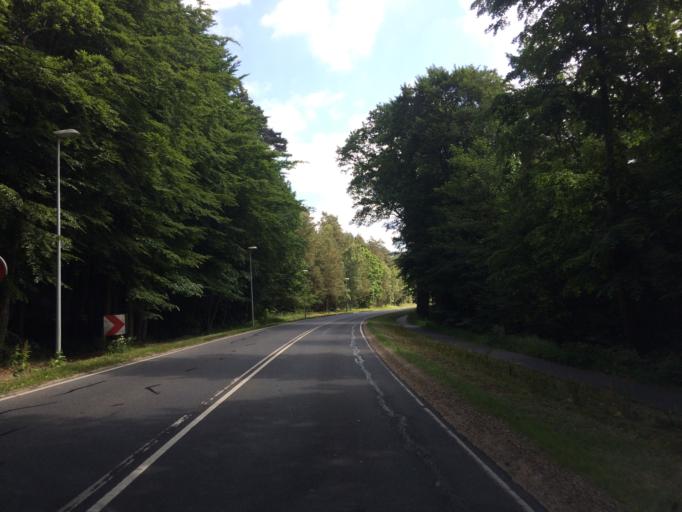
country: DK
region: Central Jutland
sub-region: Silkeborg Kommune
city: Silkeborg
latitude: 56.1629
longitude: 9.5207
